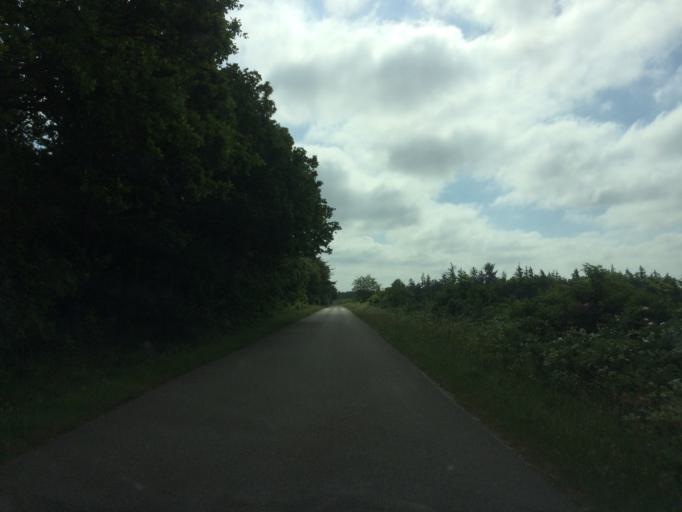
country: DK
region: Central Jutland
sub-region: Holstebro Kommune
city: Ulfborg
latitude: 56.2353
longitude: 8.4272
